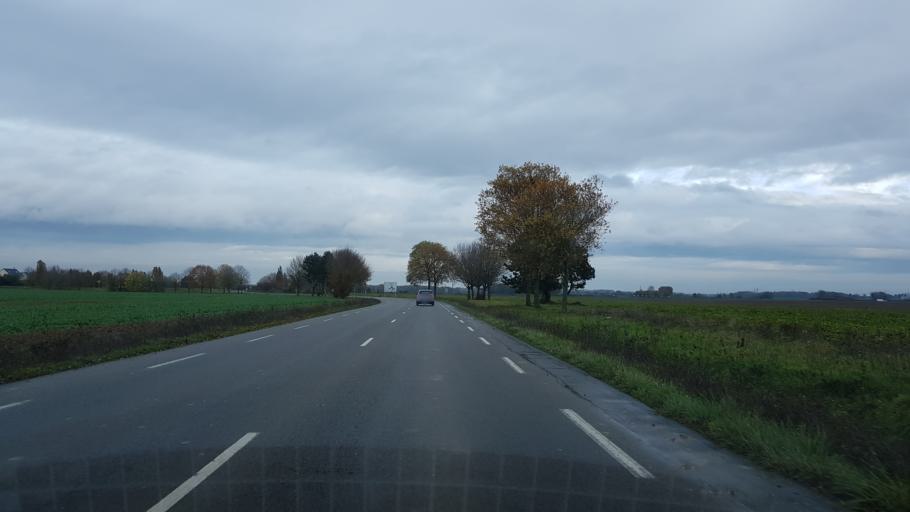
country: FR
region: Ile-de-France
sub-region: Departement de l'Essonne
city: Villiers-le-Bacle
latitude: 48.7403
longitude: 2.1147
